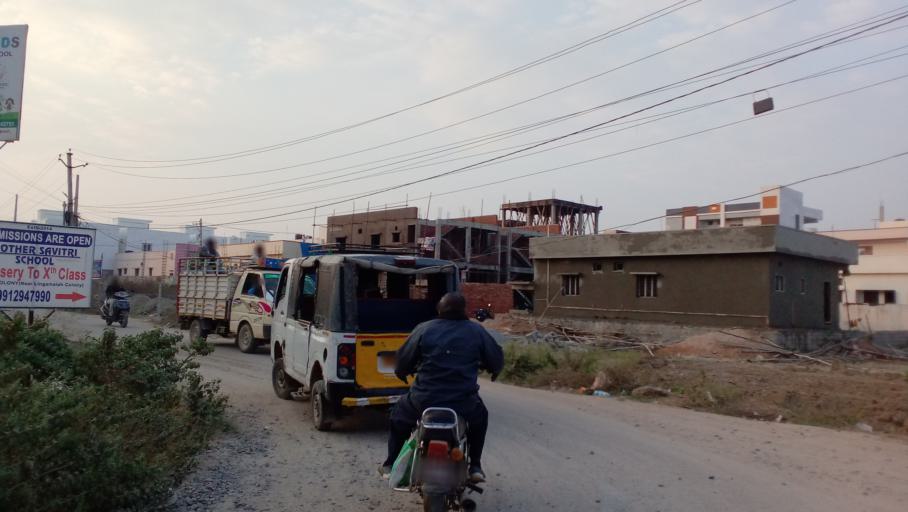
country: IN
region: Telangana
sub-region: Medak
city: Serilingampalle
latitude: 17.5178
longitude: 78.3147
